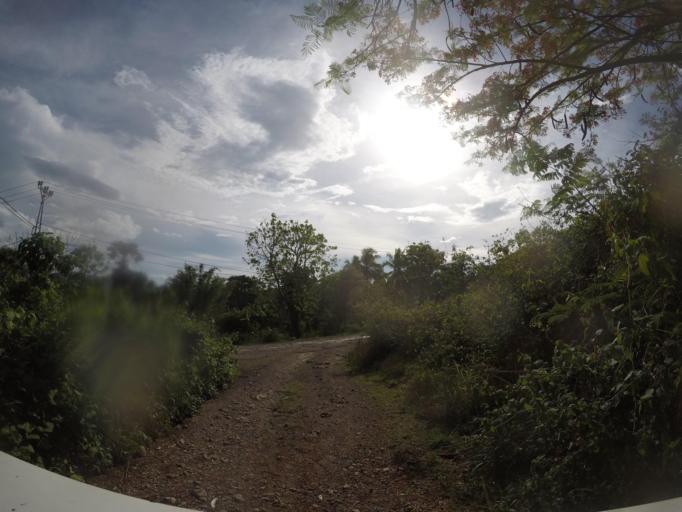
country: TL
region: Baucau
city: Baucau
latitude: -8.5082
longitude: 126.4467
